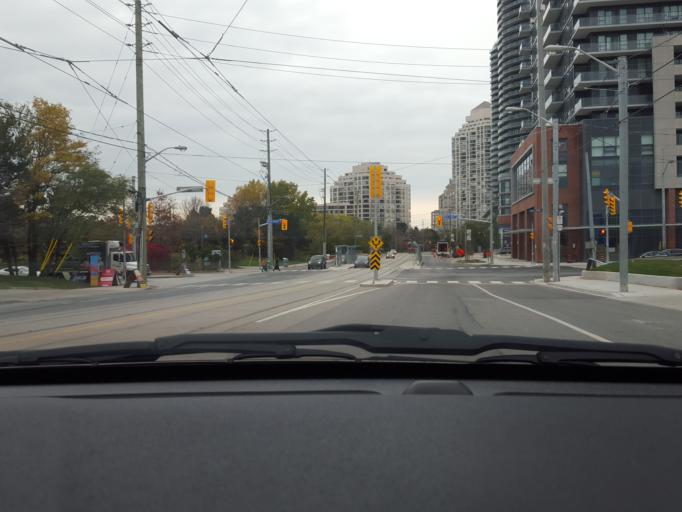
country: CA
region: Ontario
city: Etobicoke
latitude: 43.6235
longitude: -79.4810
